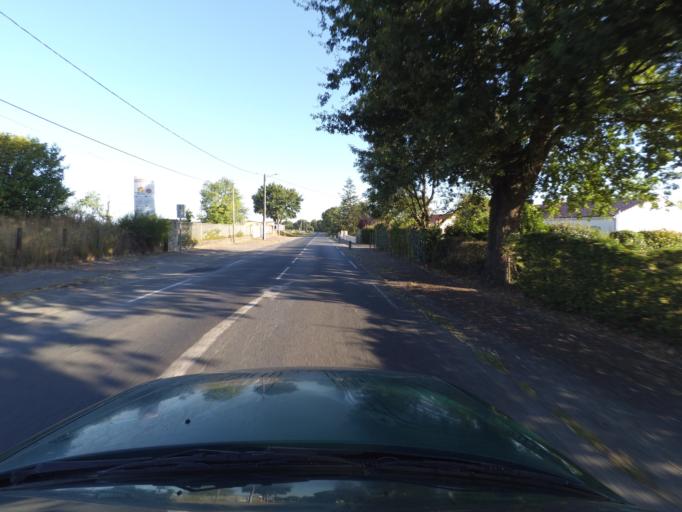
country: FR
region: Pays de la Loire
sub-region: Departement de la Loire-Atlantique
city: Vieillevigne
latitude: 46.9793
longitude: -1.4386
